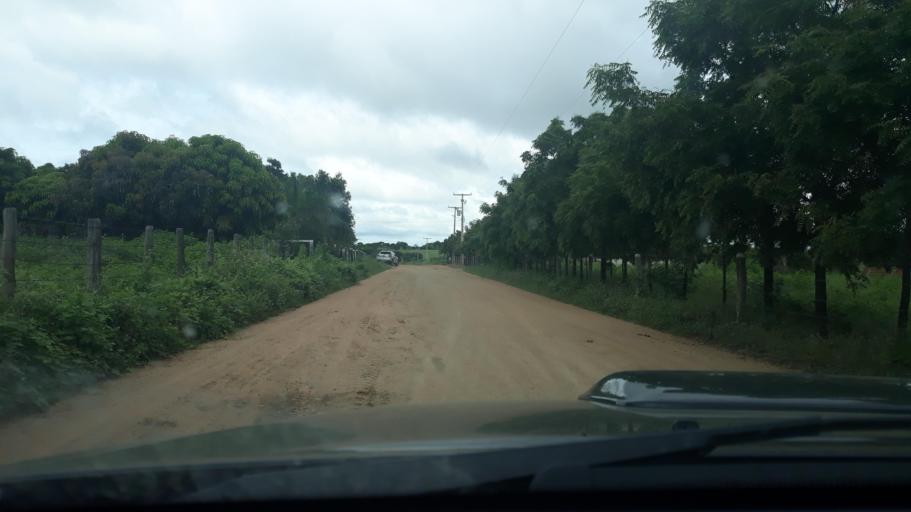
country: BR
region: Bahia
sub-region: Riacho De Santana
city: Riacho de Santana
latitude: -13.9054
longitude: -42.9018
